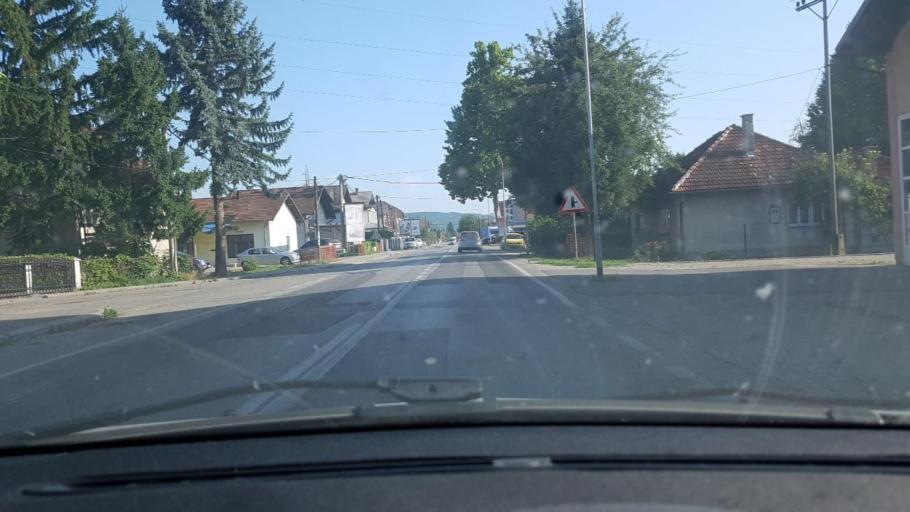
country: BA
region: Federation of Bosnia and Herzegovina
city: Bihac
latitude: 44.8231
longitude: 15.8817
